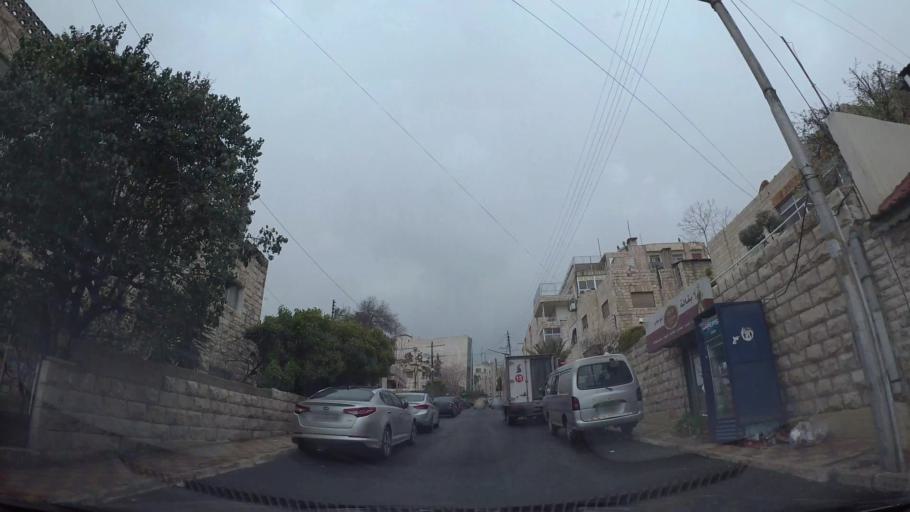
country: JO
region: Amman
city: Amman
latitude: 31.9509
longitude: 35.9105
